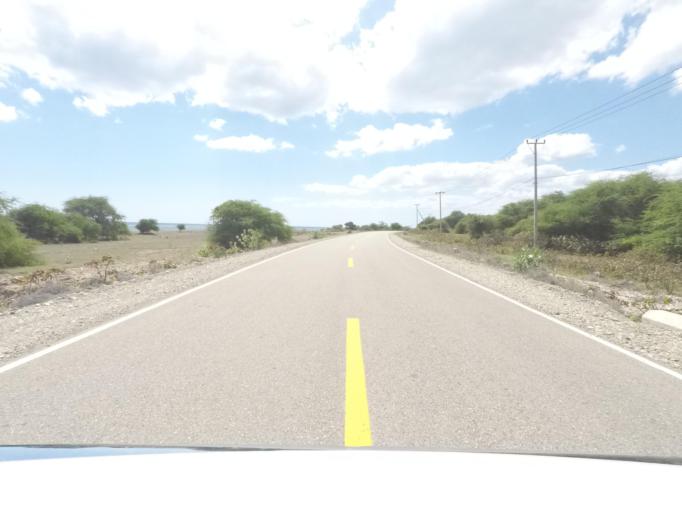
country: TL
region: Baucau
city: Baucau
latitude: -8.4142
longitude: 126.7147
